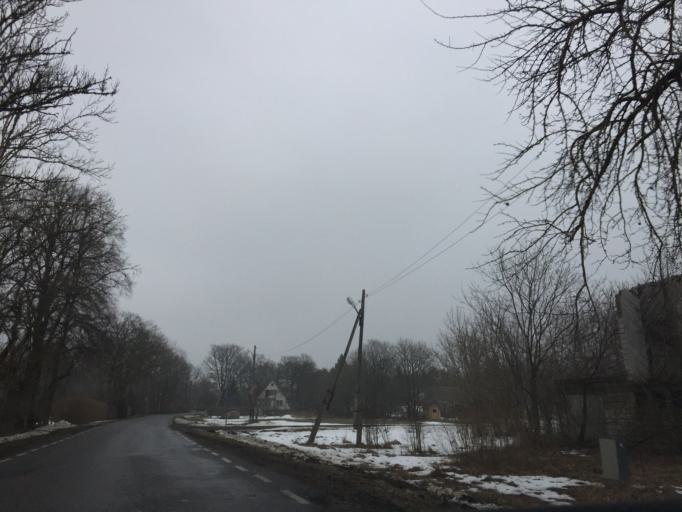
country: EE
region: Saare
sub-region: Orissaare vald
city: Orissaare
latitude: 58.4099
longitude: 22.8011
